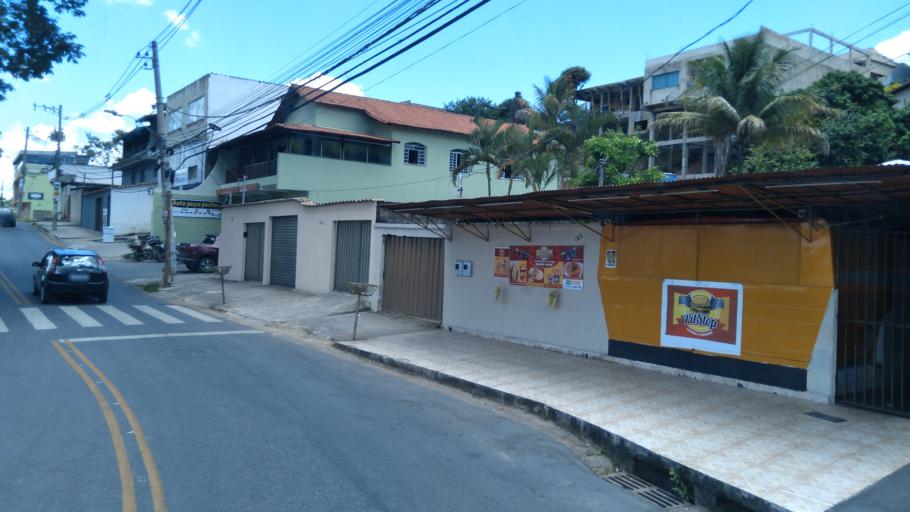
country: BR
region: Minas Gerais
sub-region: Belo Horizonte
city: Belo Horizonte
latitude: -19.8446
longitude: -43.8962
